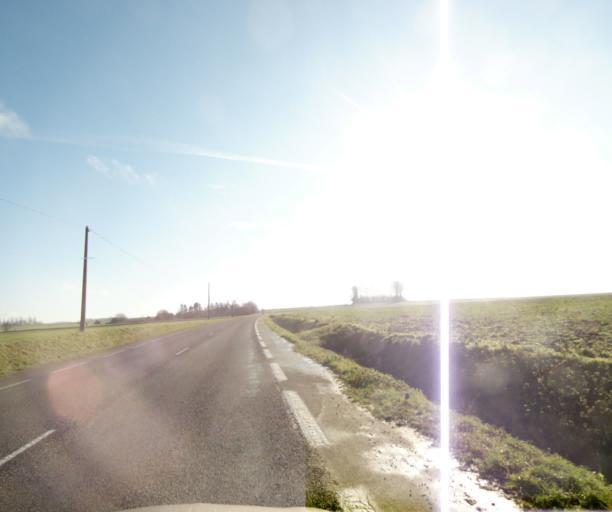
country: FR
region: Nord-Pas-de-Calais
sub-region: Departement du Nord
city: Preseau
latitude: 50.3253
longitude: 3.5623
